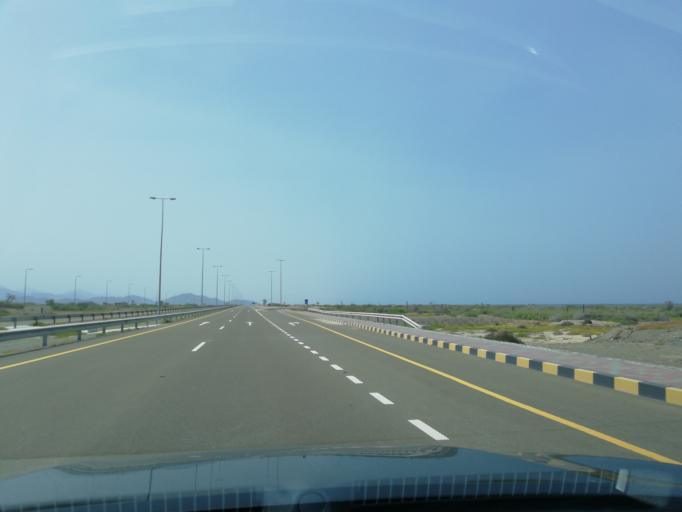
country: OM
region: Al Batinah
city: Shinas
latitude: 24.9000
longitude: 56.3969
